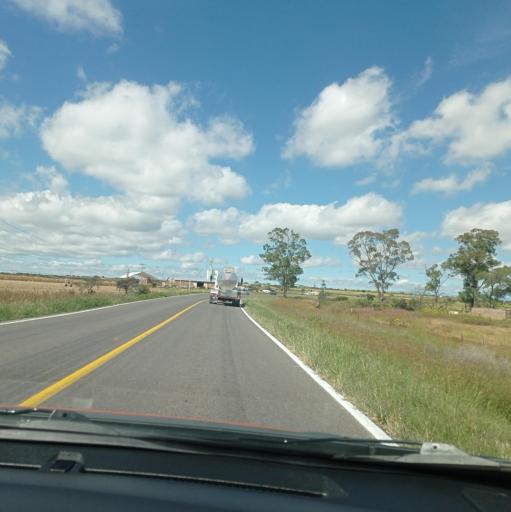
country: MX
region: Jalisco
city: Valle de Guadalupe
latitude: 21.0231
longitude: -102.5438
